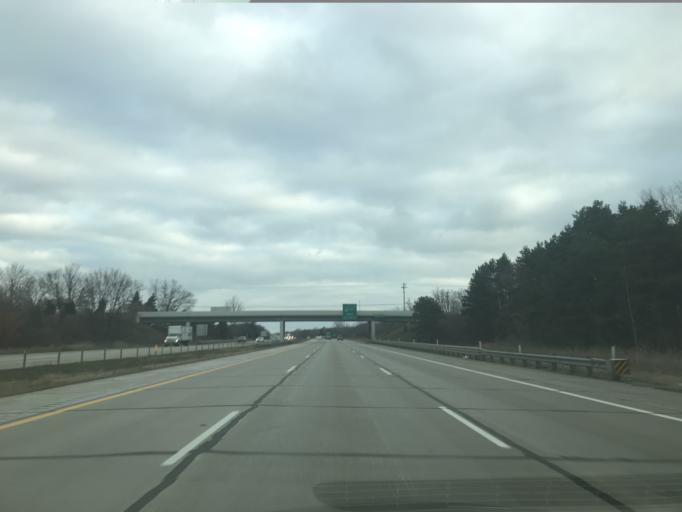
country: US
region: Michigan
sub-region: Eaton County
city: Waverly
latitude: 42.7543
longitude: -84.6675
